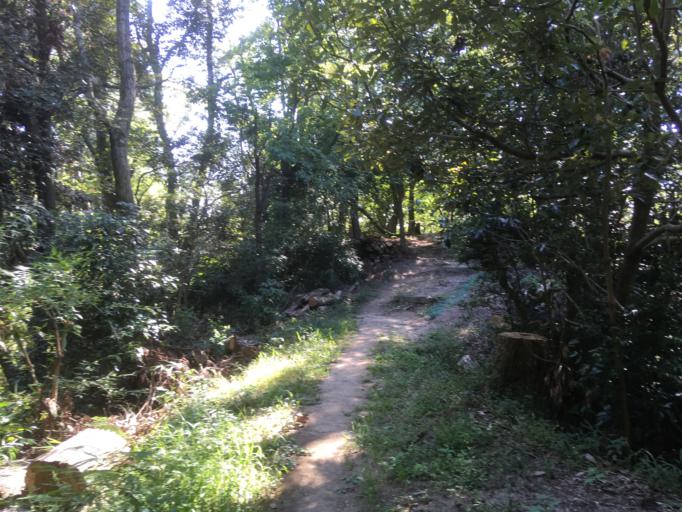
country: JP
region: Nara
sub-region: Ikoma-shi
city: Ikoma
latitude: 34.7190
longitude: 135.6705
